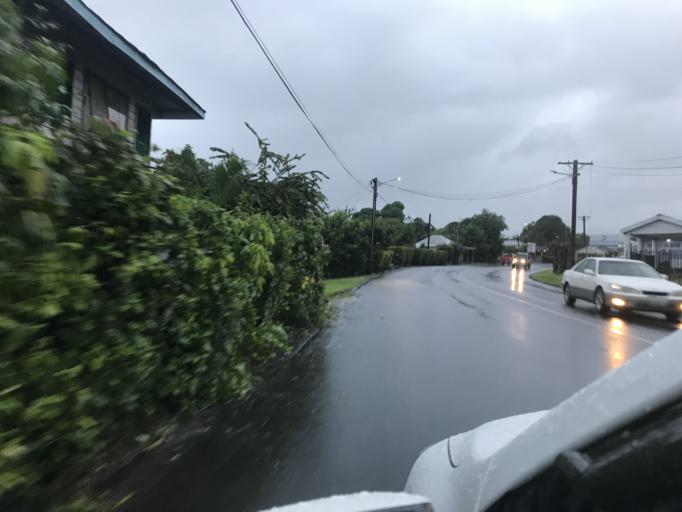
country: WS
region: Tuamasaga
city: Apia
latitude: -13.8355
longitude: -171.7637
